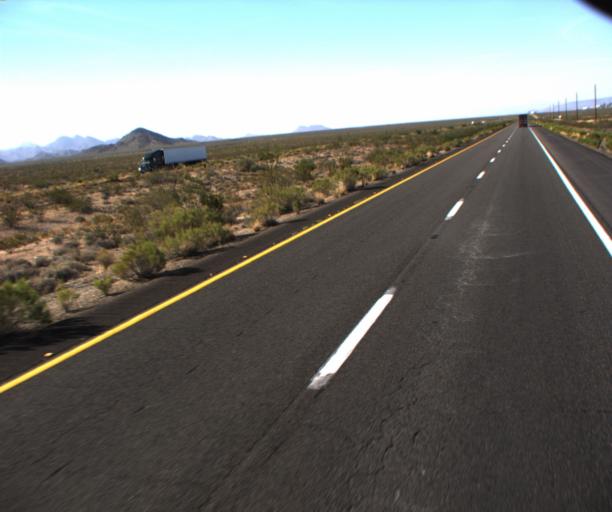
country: US
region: Arizona
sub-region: Mohave County
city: Kingman
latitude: 35.0968
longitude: -114.1190
